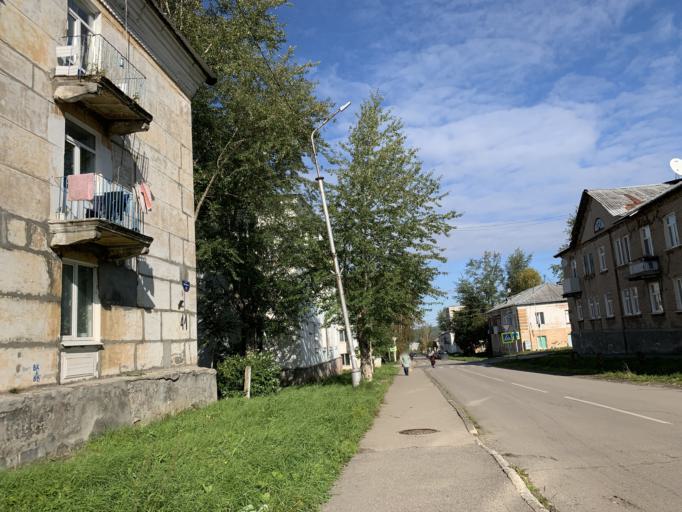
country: RU
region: Perm
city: Gubakha
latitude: 58.8400
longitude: 57.5554
